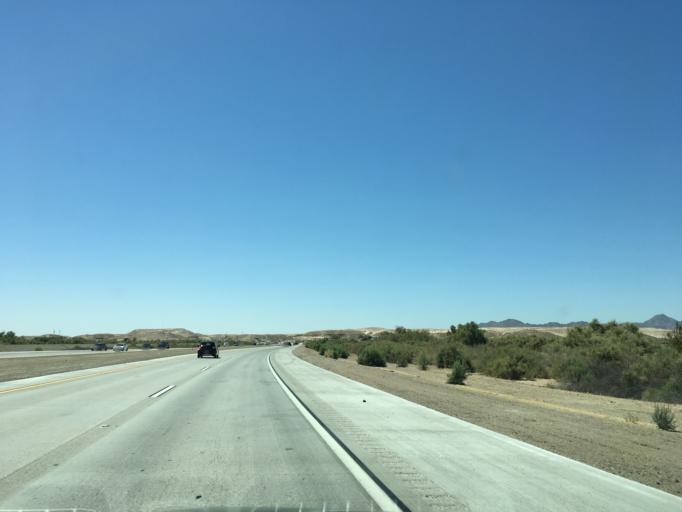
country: MX
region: Baja California
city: Los Algodones
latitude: 32.7422
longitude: -114.6861
